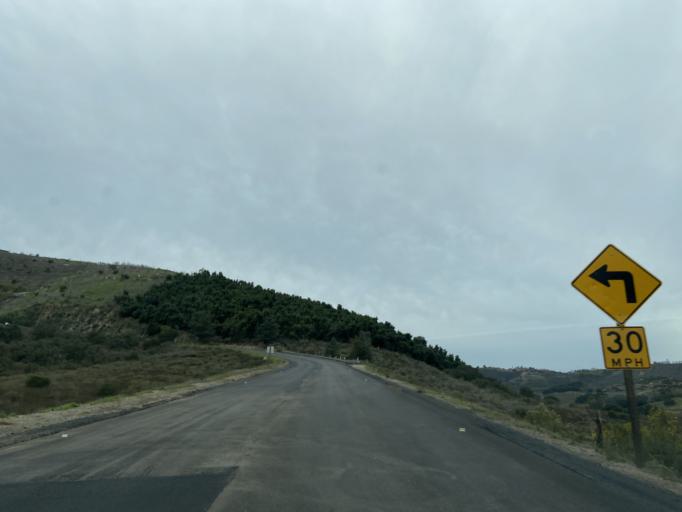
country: US
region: California
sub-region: San Diego County
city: Valley Center
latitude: 33.3078
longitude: -117.0174
